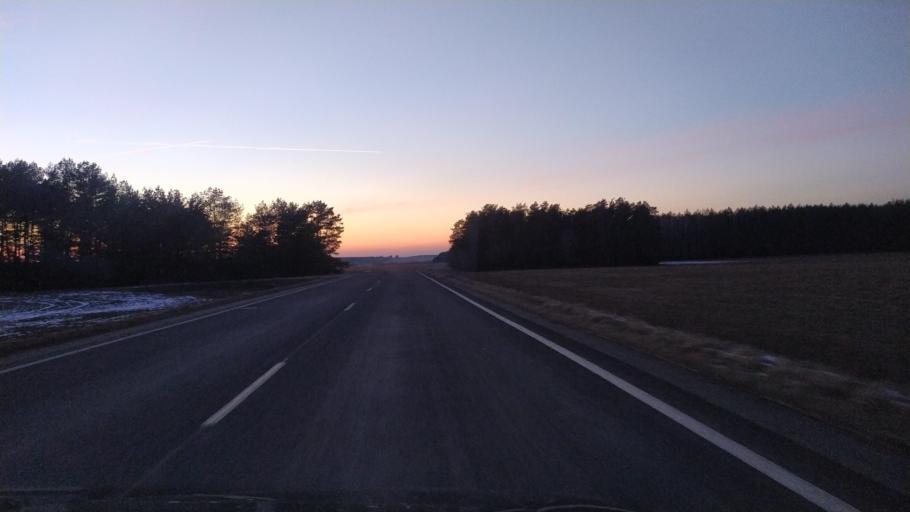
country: BY
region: Brest
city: Kamyanyets
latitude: 52.3952
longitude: 23.9259
